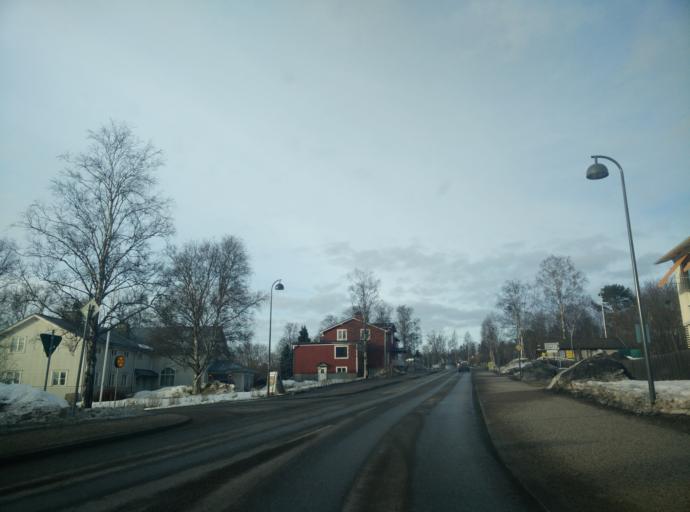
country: SE
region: Vaesternorrland
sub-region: Sundsvalls Kommun
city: Johannedal
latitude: 62.4292
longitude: 17.4163
